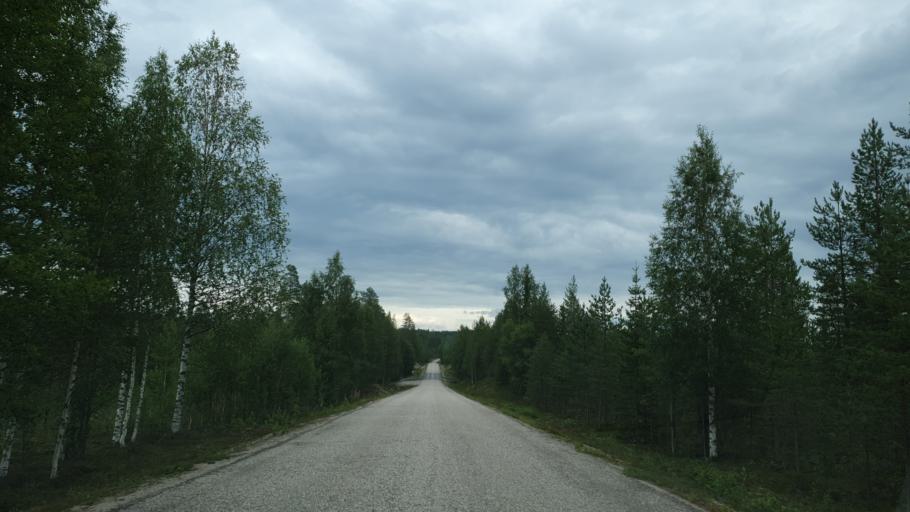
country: FI
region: Kainuu
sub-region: Kehys-Kainuu
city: Kuhmo
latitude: 64.3399
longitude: 29.3219
